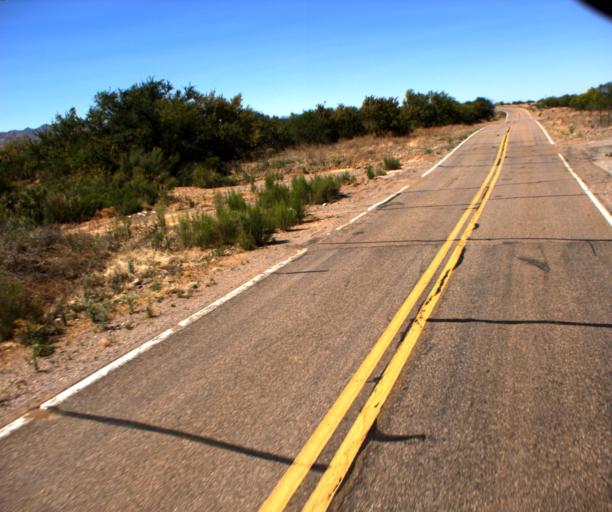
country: US
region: Arizona
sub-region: Pima County
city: Arivaca Junction
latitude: 31.6800
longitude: -111.4865
